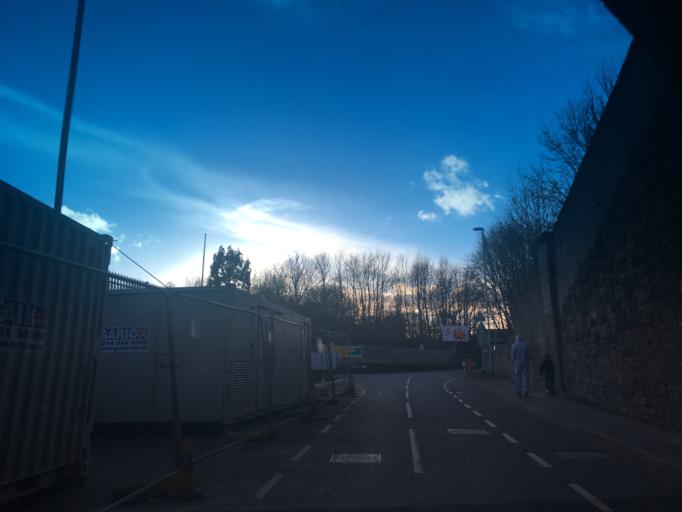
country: GB
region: England
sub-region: City and Borough of Leeds
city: Leeds
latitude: 53.7899
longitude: -1.5766
